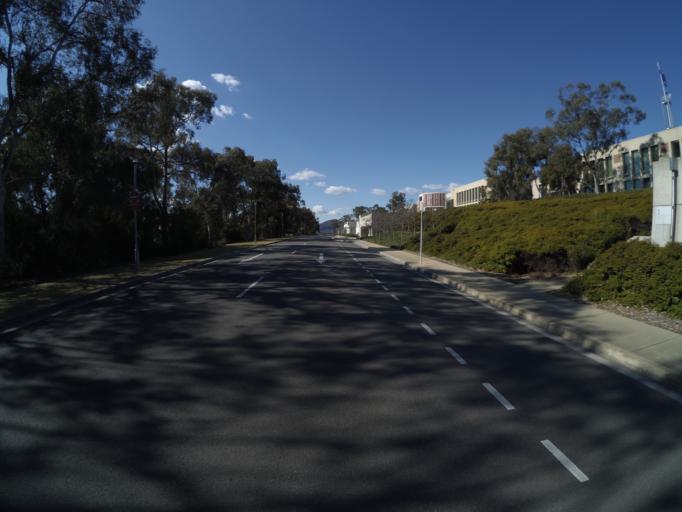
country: AU
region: Australian Capital Territory
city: Forrest
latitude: -35.3079
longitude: 149.1221
